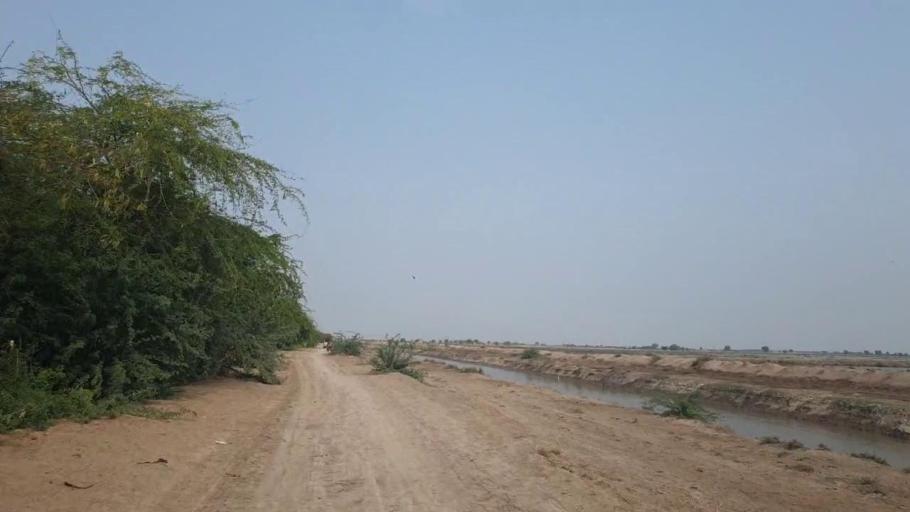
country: PK
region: Sindh
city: Badin
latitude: 24.7197
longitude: 68.7705
